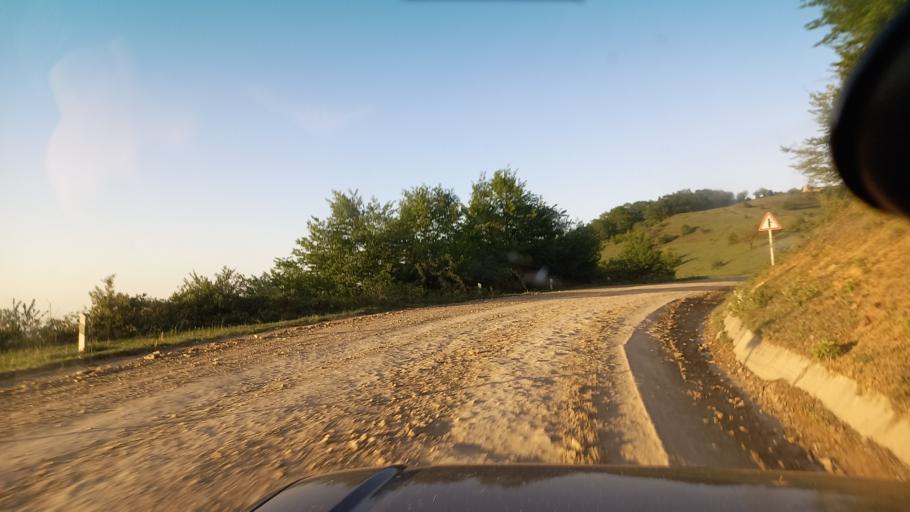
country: RU
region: Dagestan
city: Khuchni
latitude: 41.9999
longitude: 47.9721
